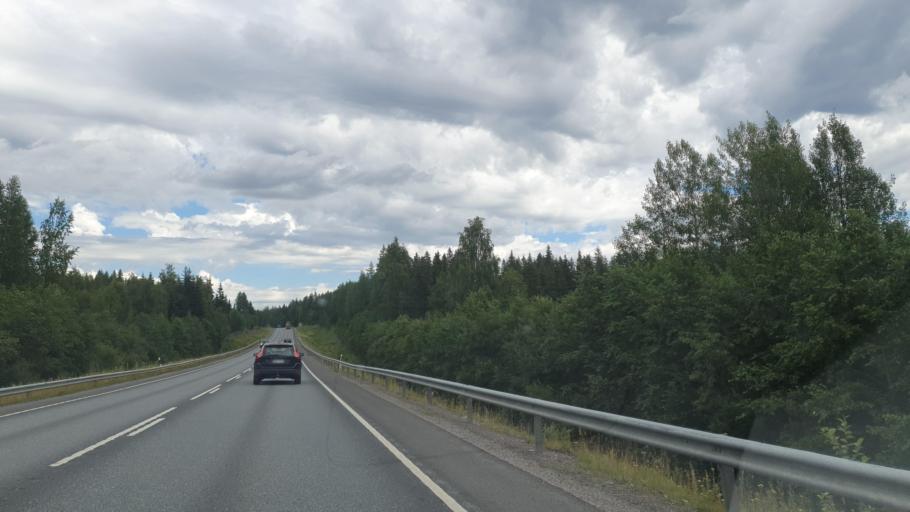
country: FI
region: Pirkanmaa
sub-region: Tampere
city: Kuhmalahti
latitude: 61.7365
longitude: 24.7855
